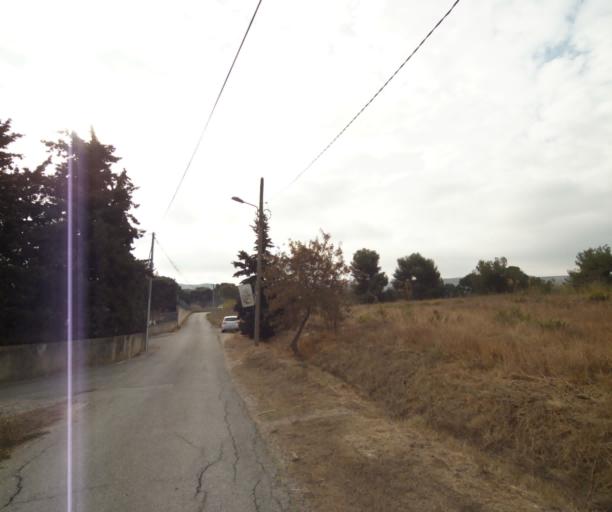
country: FR
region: Provence-Alpes-Cote d'Azur
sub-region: Departement des Bouches-du-Rhone
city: Gignac-la-Nerthe
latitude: 43.4039
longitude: 5.2673
